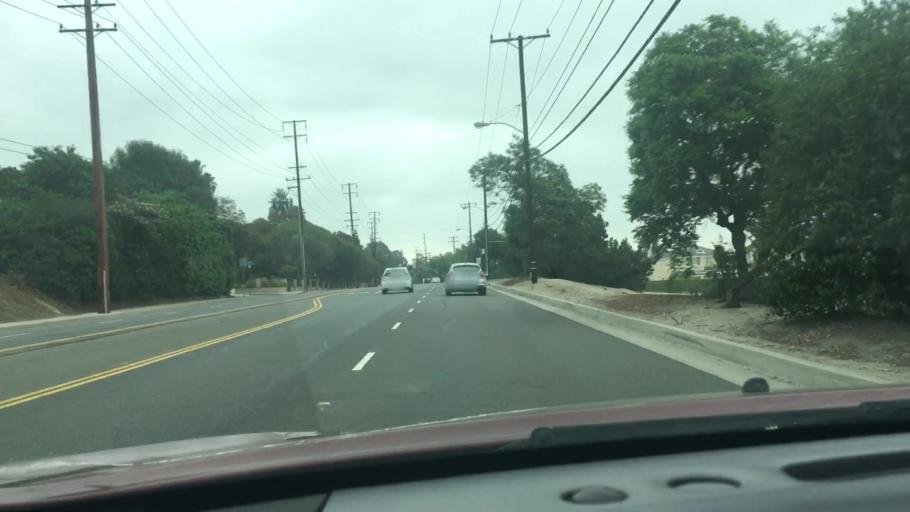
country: US
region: California
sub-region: Orange County
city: Buena Park
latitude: 33.8778
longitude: -117.9841
